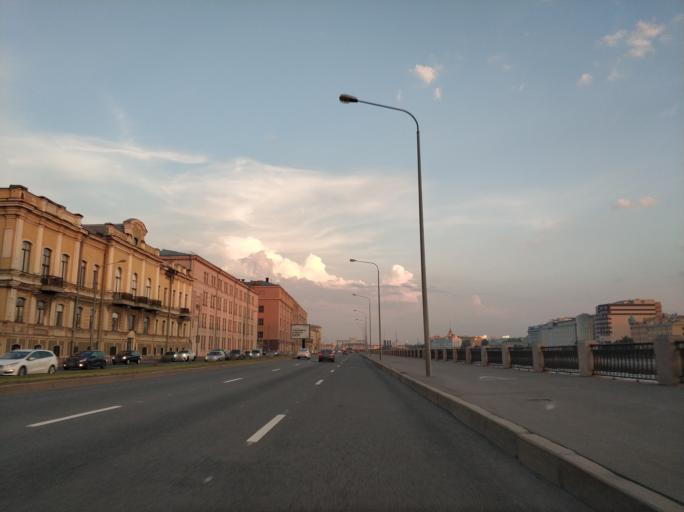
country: RU
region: Leningrad
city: Sampsonievskiy
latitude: 59.9646
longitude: 30.3375
